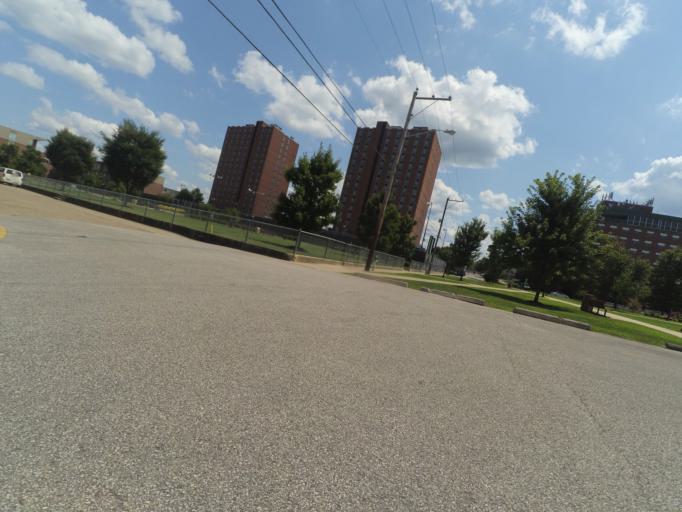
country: US
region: West Virginia
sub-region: Cabell County
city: Huntington
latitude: 38.4237
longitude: -82.4263
